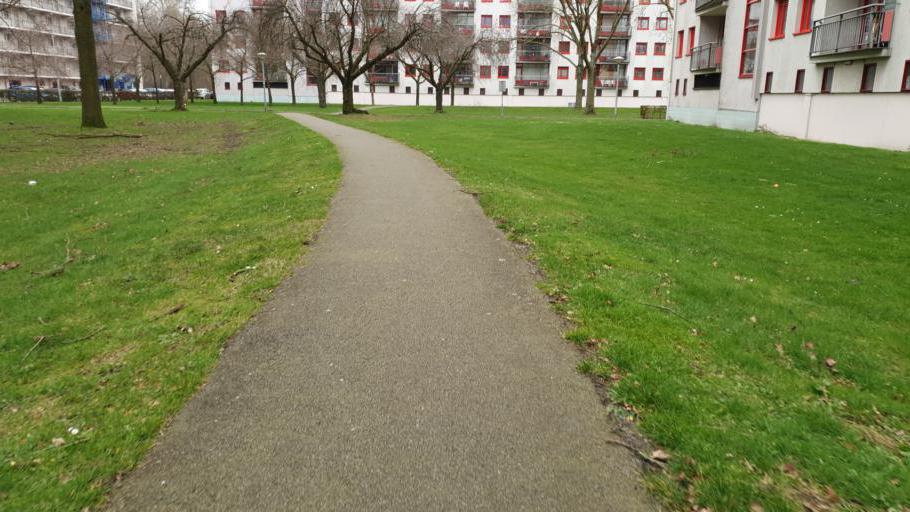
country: NL
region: North Brabant
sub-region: Gemeente Eindhoven
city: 't Hofke
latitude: 51.4527
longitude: 5.5224
